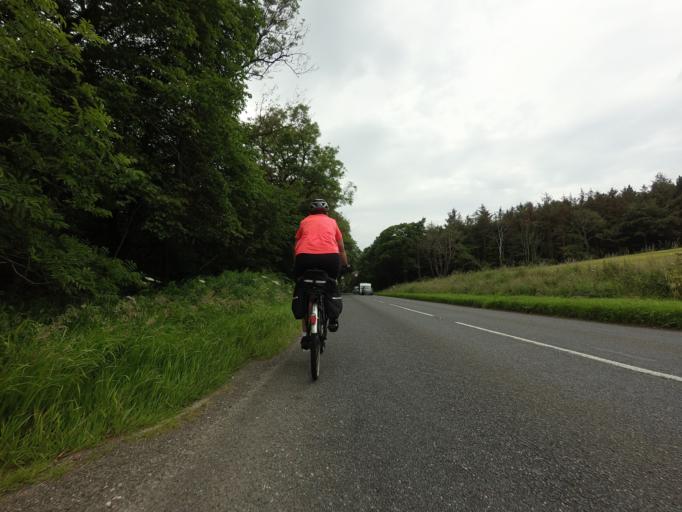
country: GB
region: Scotland
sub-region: Aberdeenshire
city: Portsoy
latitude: 57.6749
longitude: -2.7129
